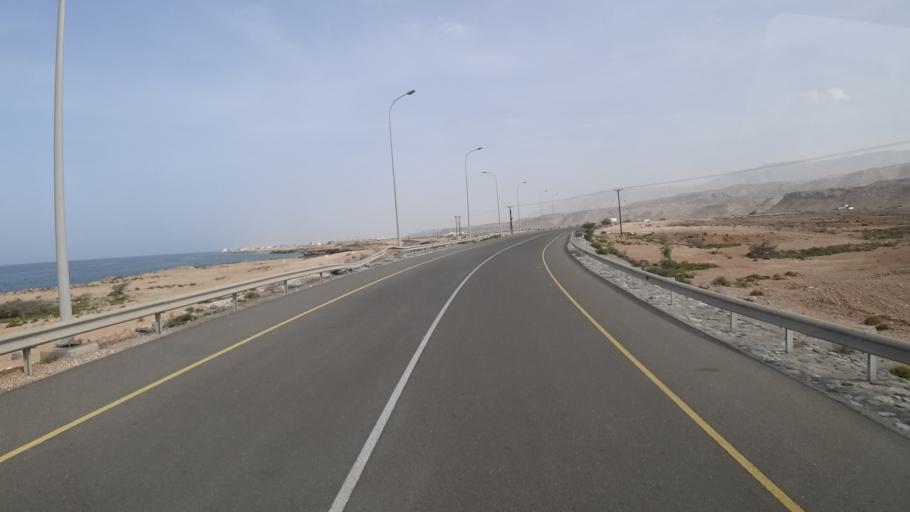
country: OM
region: Ash Sharqiyah
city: Sur
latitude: 23.0039
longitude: 59.1172
